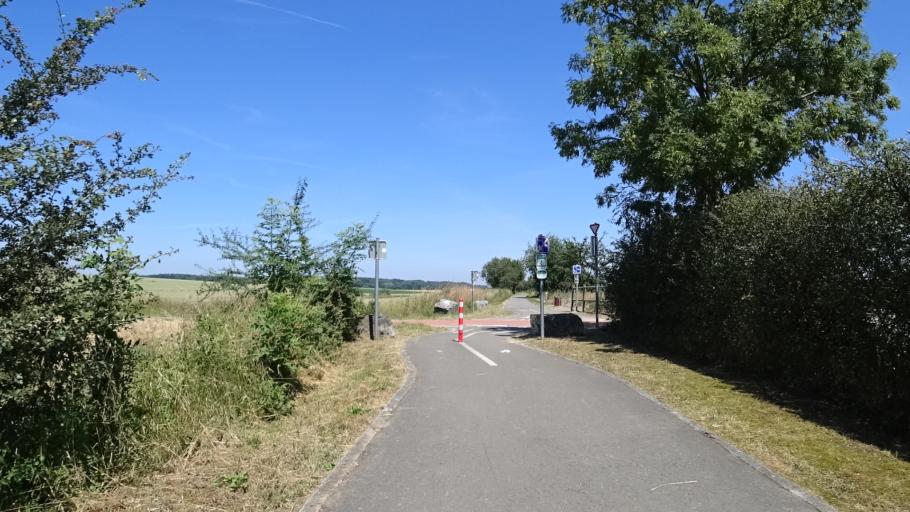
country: BE
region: Wallonia
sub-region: Province du Brabant Wallon
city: Walhain-Saint-Paul
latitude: 50.5943
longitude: 4.7307
